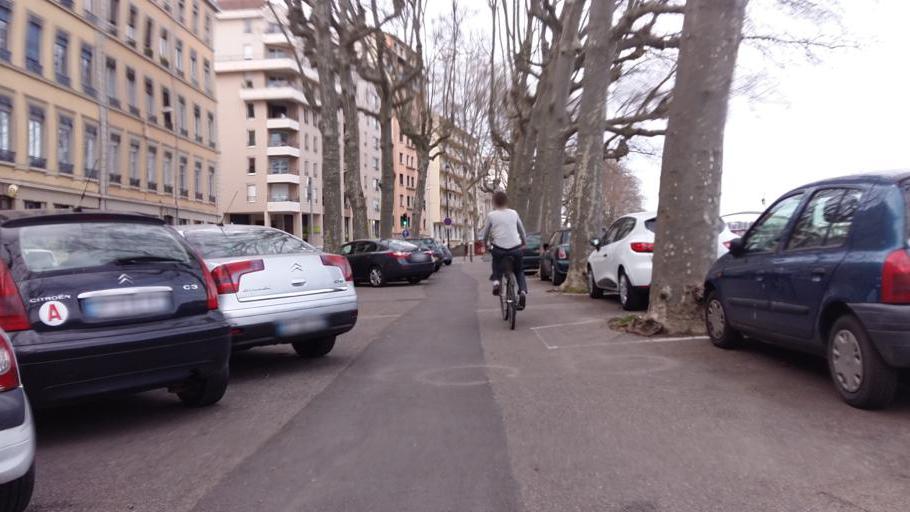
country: FR
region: Rhone-Alpes
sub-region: Departement du Rhone
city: Tassin-la-Demi-Lune
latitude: 45.7778
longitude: 4.8079
